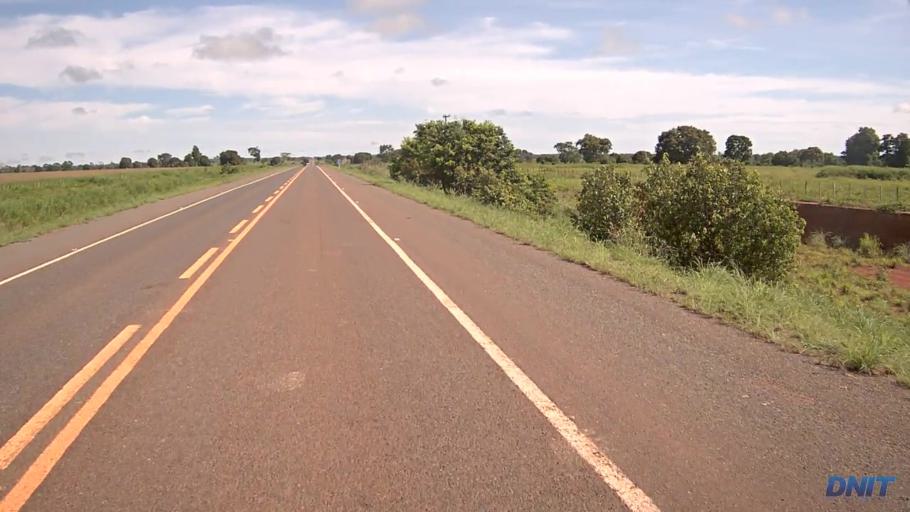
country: BR
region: Goias
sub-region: Sao Miguel Do Araguaia
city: Sao Miguel do Araguaia
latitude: -13.3914
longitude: -50.1377
